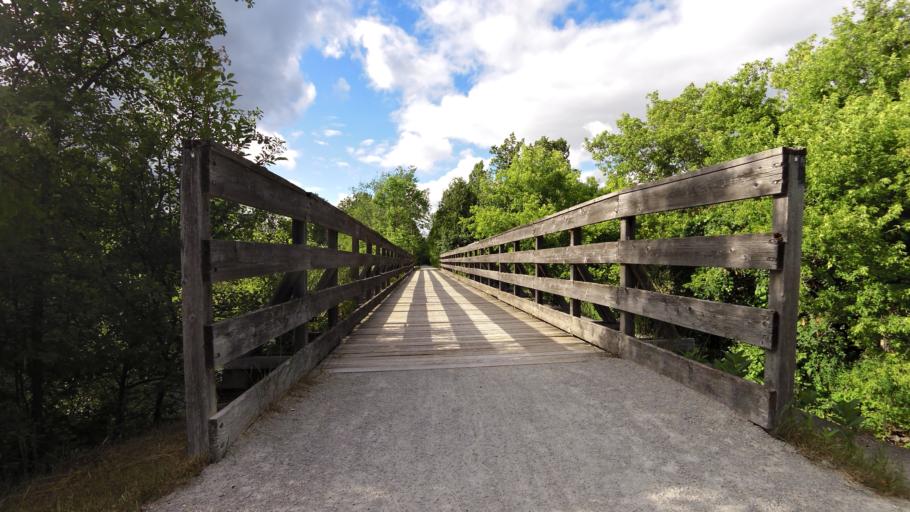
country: CA
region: Ontario
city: Orangeville
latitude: 43.8058
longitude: -79.9324
